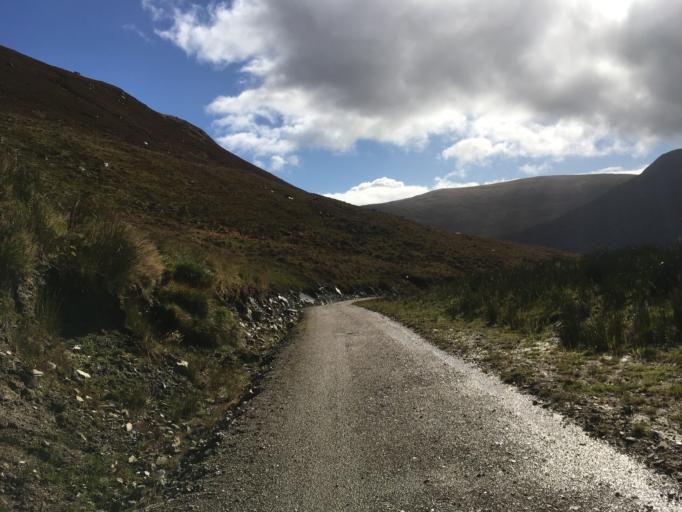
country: GB
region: Scotland
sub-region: Highland
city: Spean Bridge
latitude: 57.3482
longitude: -4.9827
